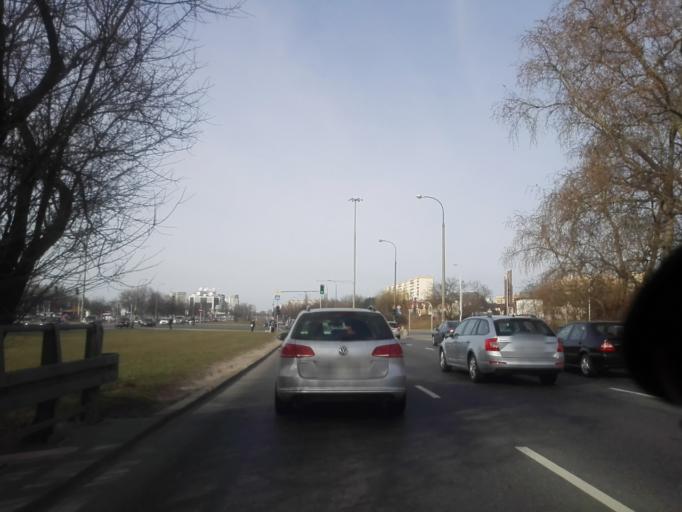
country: PL
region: Masovian Voivodeship
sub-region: Warszawa
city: Mokotow
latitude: 52.1741
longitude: 21.0442
